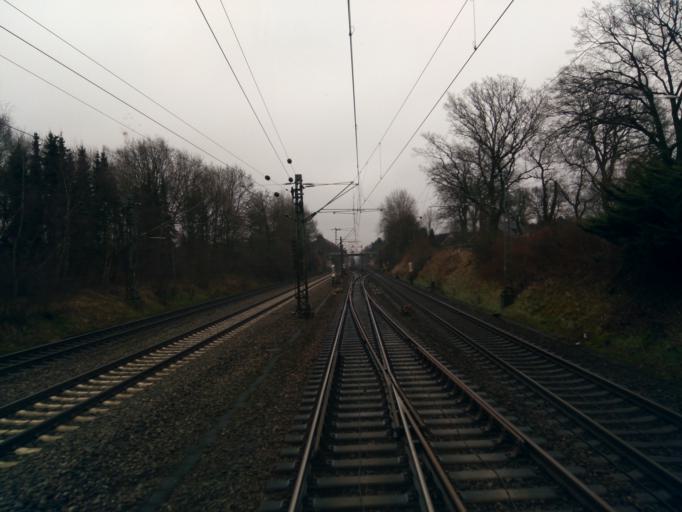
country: DE
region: Lower Saxony
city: Tostedt
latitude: 53.2761
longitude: 9.7411
